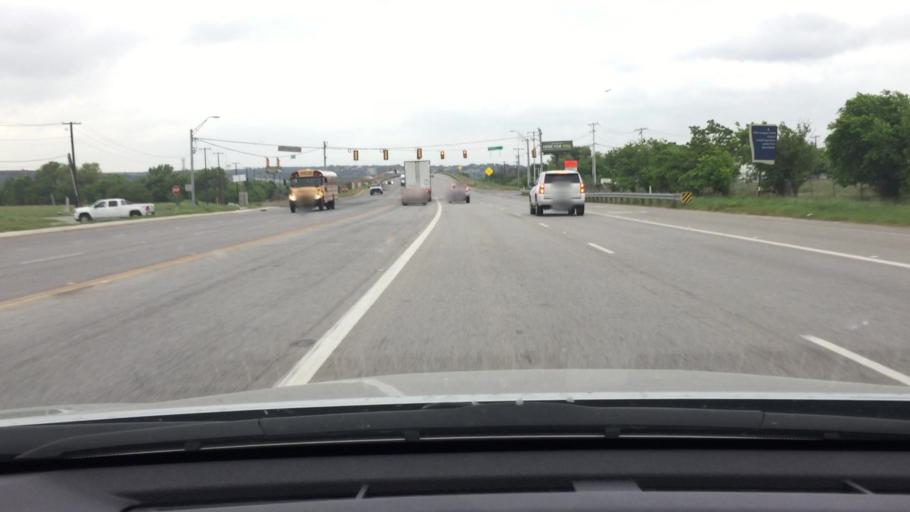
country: US
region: Texas
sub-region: Comal County
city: New Braunfels
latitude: 29.6778
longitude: -98.1549
